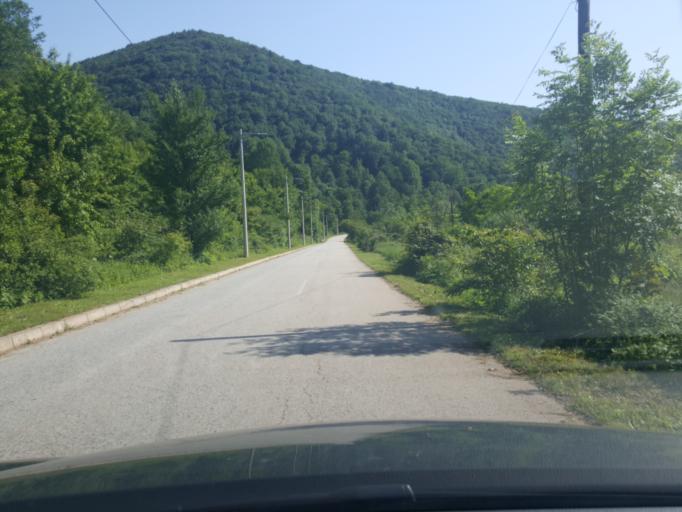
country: RS
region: Central Serbia
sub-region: Nisavski Okrug
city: Razanj
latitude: 43.8622
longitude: 21.6253
